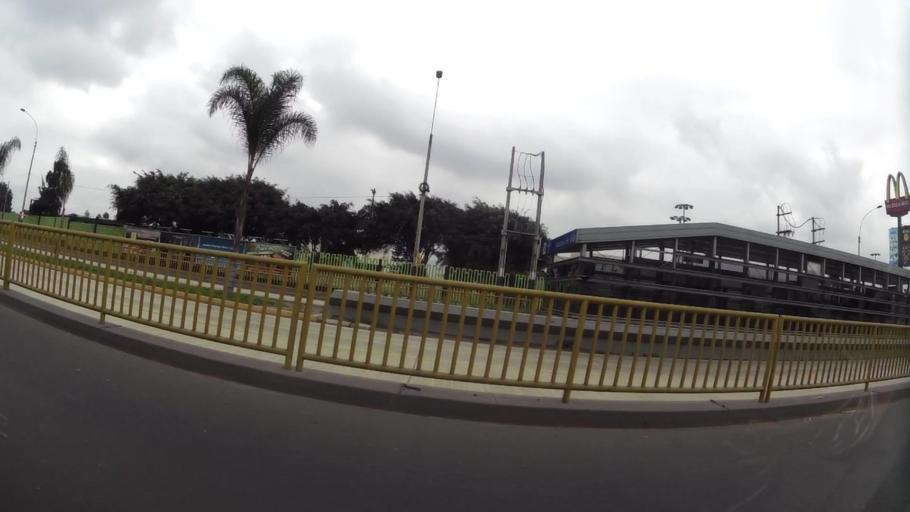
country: PE
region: Lima
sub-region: Lima
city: Surco
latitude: -12.1728
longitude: -77.0155
